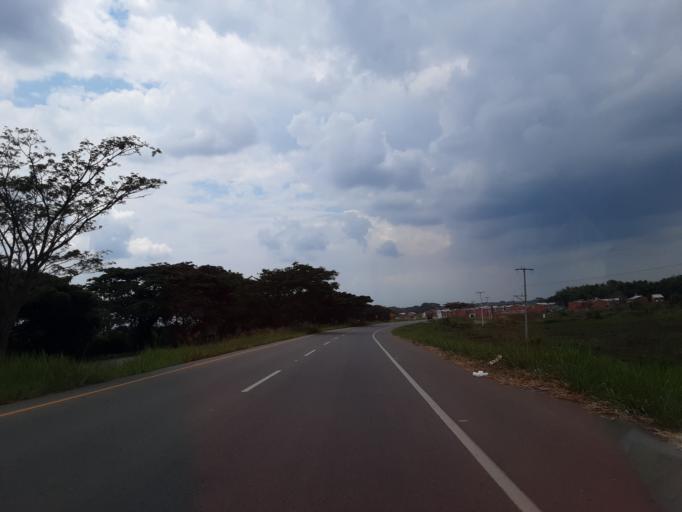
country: CO
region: Cauca
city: Santander de Quilichao
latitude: 3.0288
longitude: -76.4813
